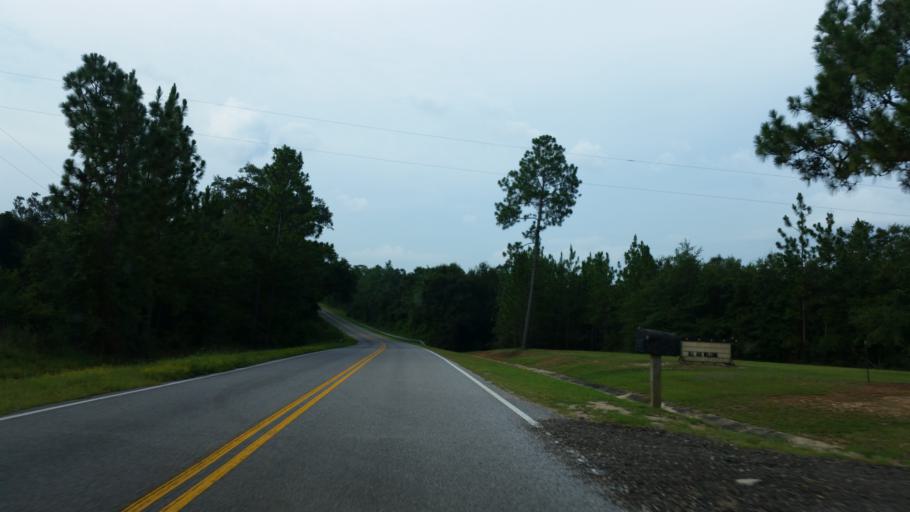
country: US
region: Florida
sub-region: Escambia County
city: Molino
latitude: 30.7826
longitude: -87.5246
